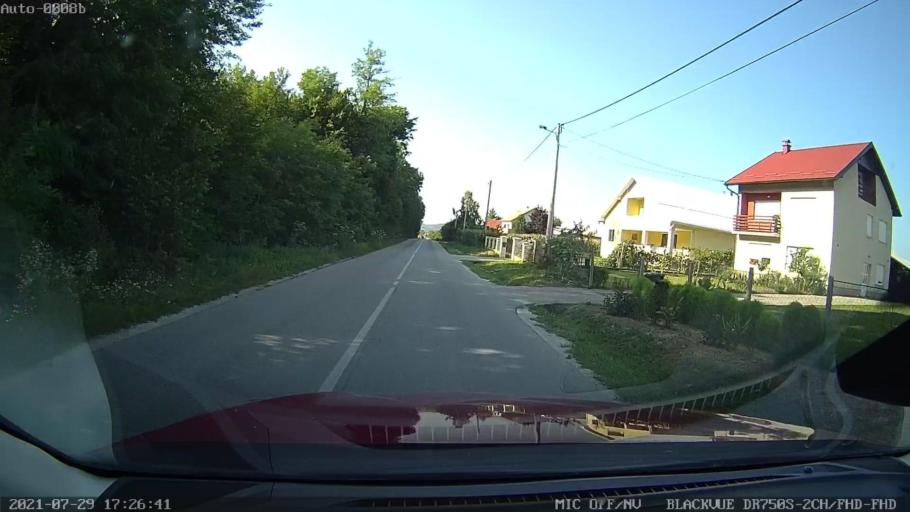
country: HR
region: Varazdinska
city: Ivanec
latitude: 46.2555
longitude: 16.1175
